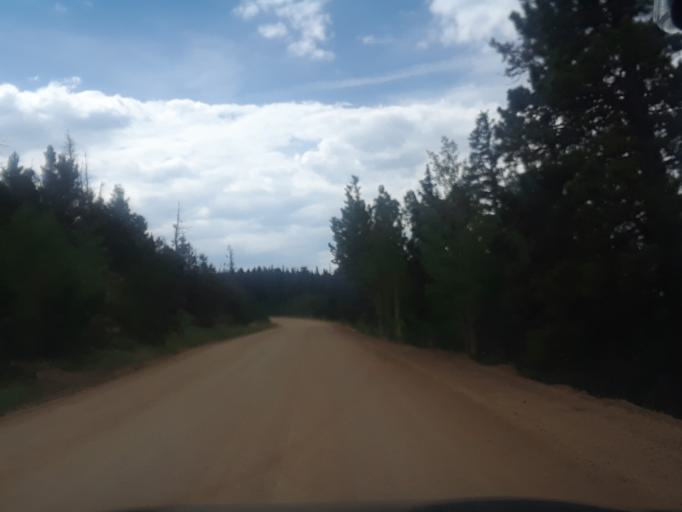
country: US
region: Colorado
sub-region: Boulder County
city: Nederland
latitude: 40.0436
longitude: -105.5167
